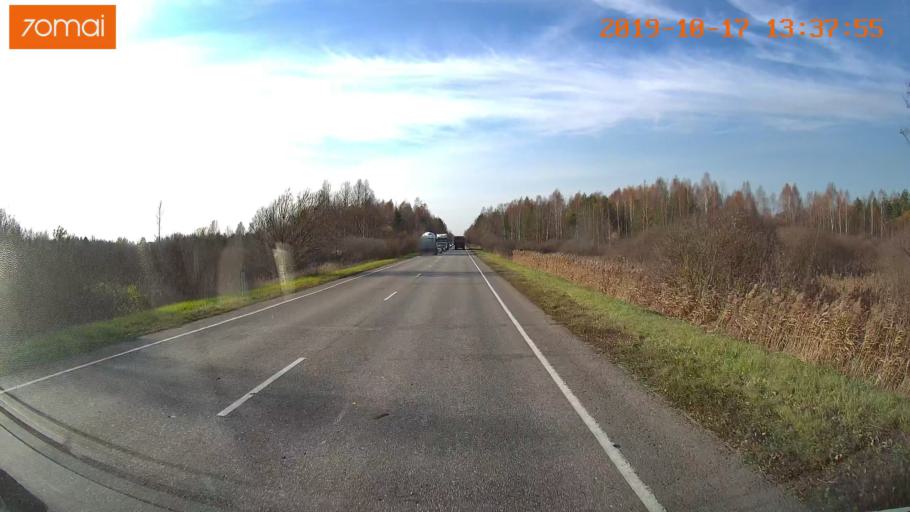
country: RU
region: Rjazan
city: Tuma
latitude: 55.1427
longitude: 40.6268
